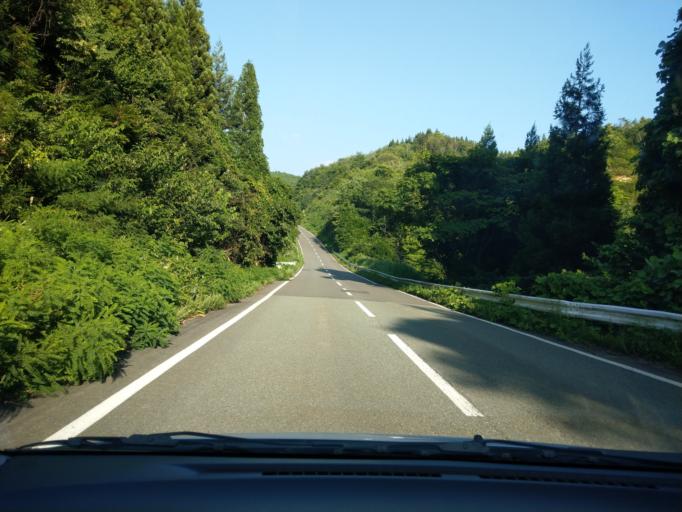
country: JP
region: Akita
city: Akita
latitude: 39.5694
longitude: 140.2320
